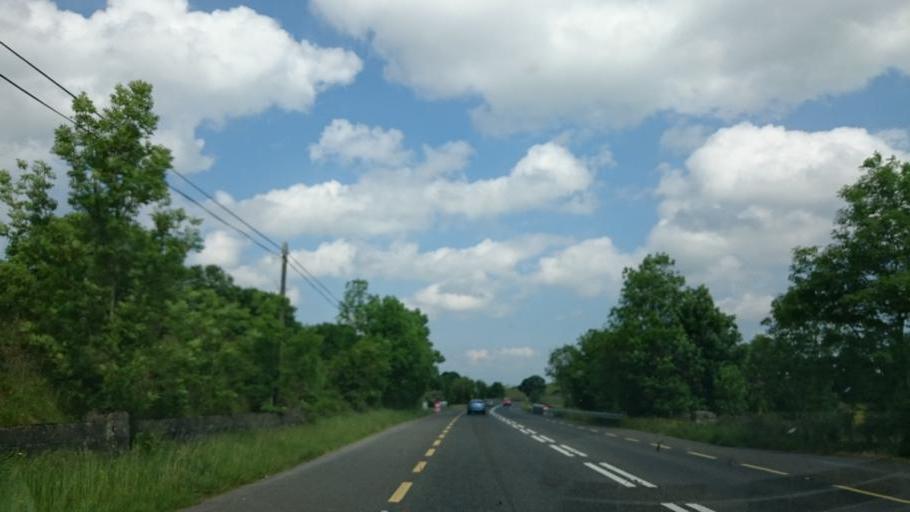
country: IE
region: Connaught
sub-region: Sligo
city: Tobercurry
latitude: 53.9345
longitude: -8.7868
